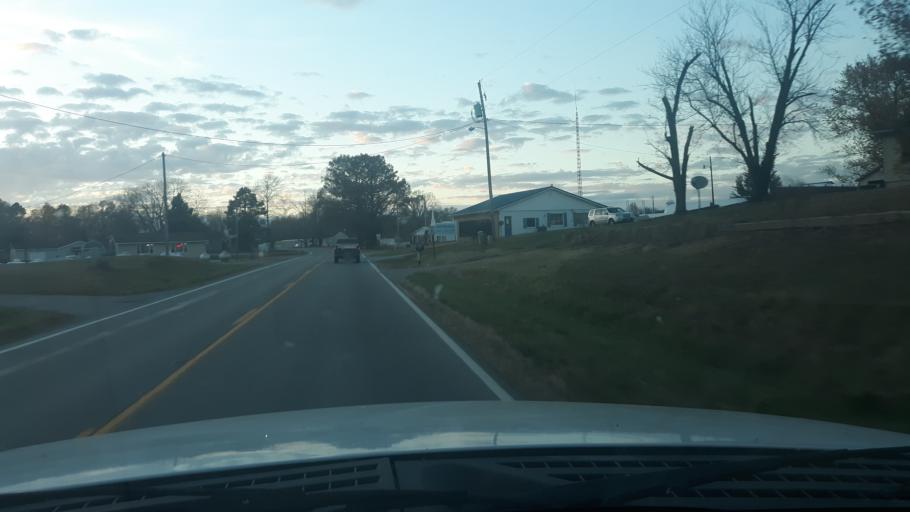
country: US
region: Illinois
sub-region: Saline County
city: Harrisburg
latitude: 37.8398
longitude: -88.6012
